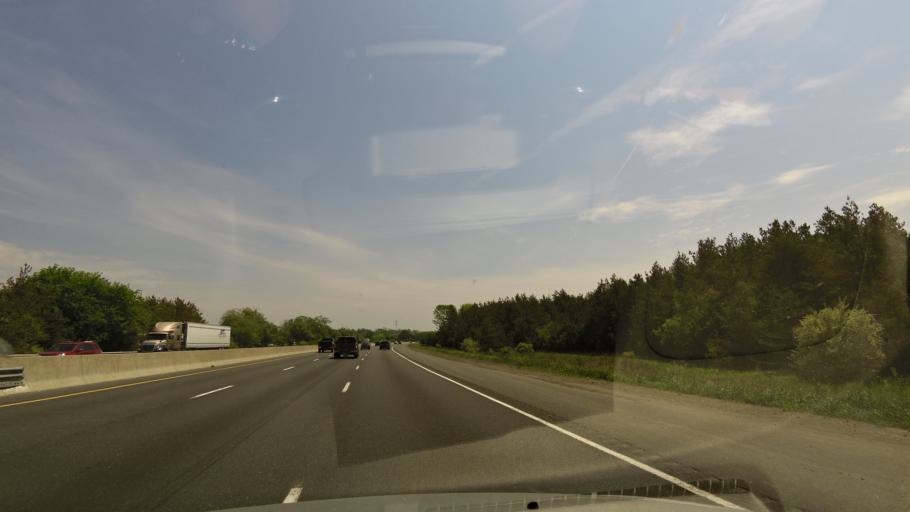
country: CA
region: Ontario
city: Oshawa
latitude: 43.8865
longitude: -78.8205
